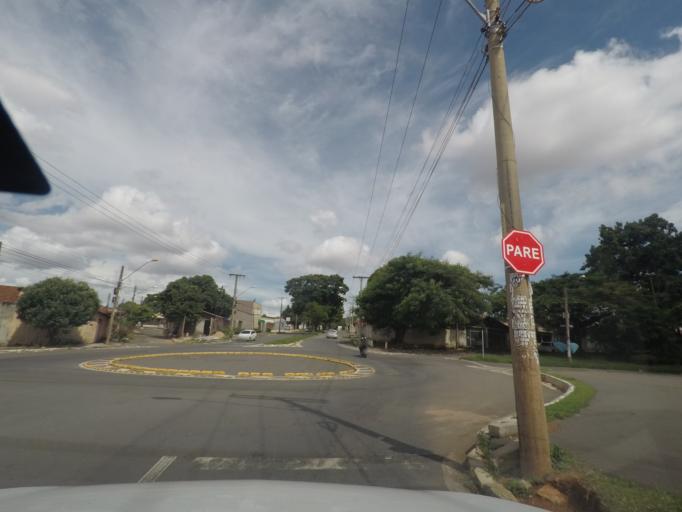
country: BR
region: Goias
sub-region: Goiania
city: Goiania
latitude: -16.7205
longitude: -49.3249
